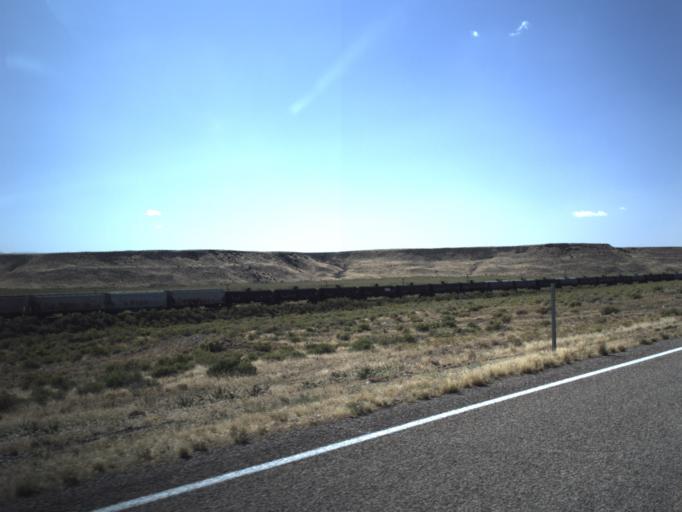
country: US
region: Utah
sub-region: Beaver County
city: Milford
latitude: 38.7469
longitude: -112.9523
